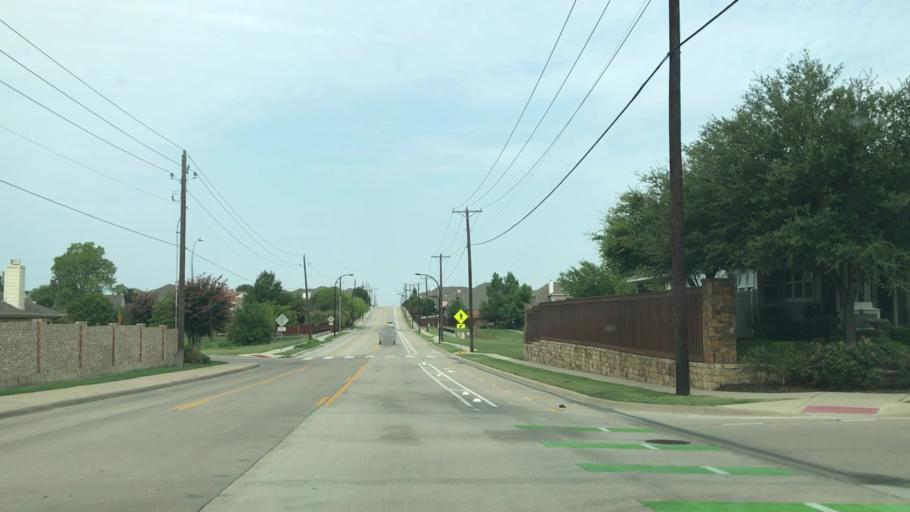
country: US
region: Texas
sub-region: Tarrant County
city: Keller
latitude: 32.9020
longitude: -97.2764
